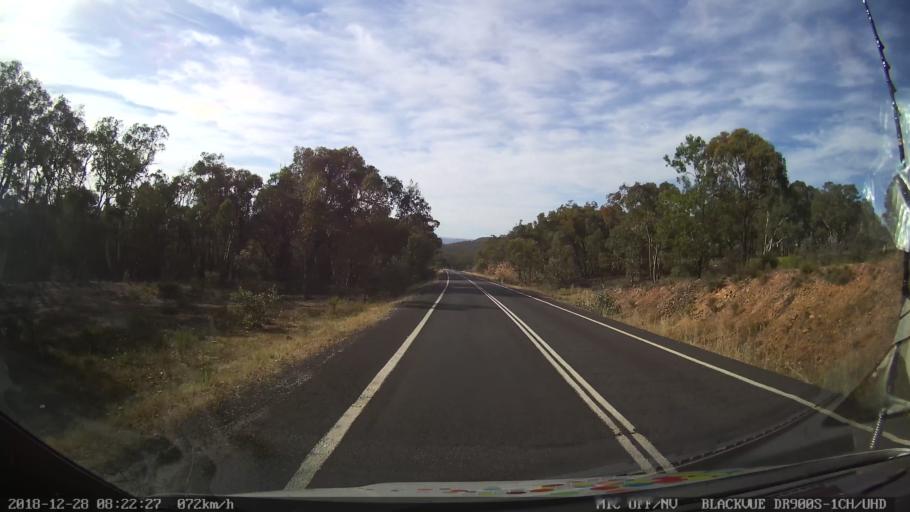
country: AU
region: New South Wales
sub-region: Blayney
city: Blayney
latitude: -33.8934
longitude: 149.3482
